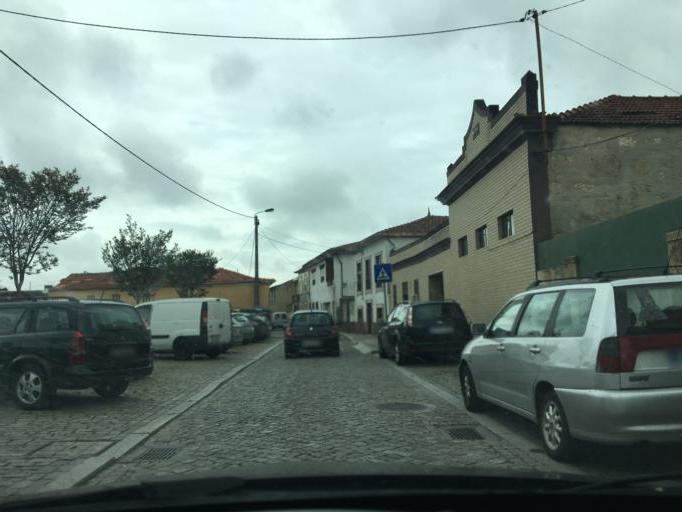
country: PT
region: Porto
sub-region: Matosinhos
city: Santa Cruz do Bispo
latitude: 41.2229
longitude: -8.6769
